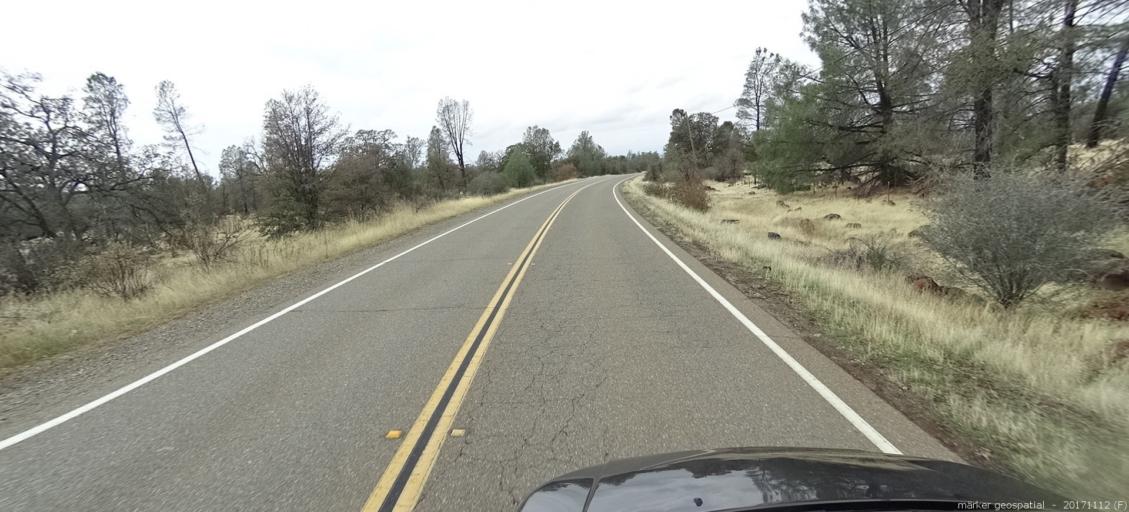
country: US
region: California
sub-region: Shasta County
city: Palo Cedro
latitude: 40.4814
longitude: -122.1056
